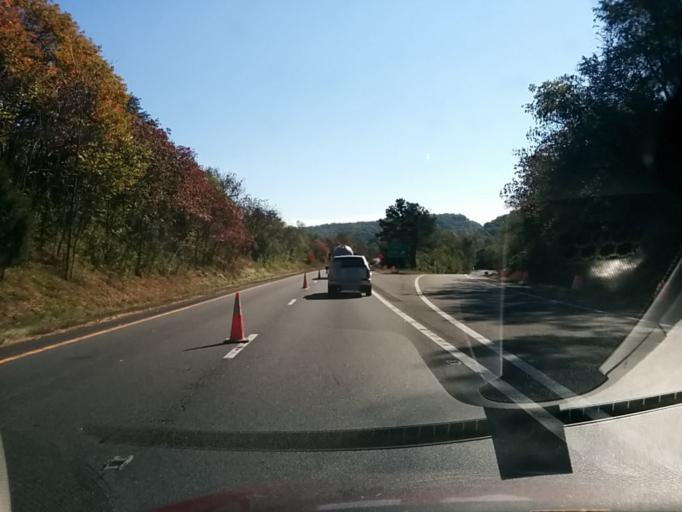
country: US
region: Virginia
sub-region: Albemarle County
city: Crozet
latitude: 38.0349
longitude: -78.6067
